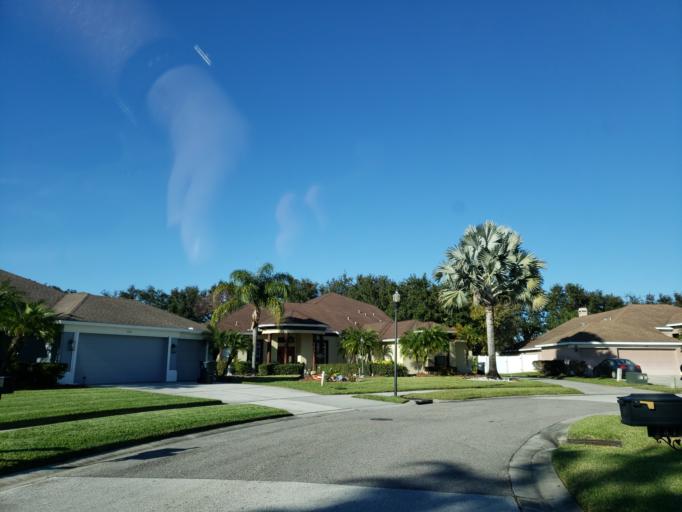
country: US
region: Florida
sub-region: Hillsborough County
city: Bloomingdale
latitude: 27.9039
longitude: -82.2054
